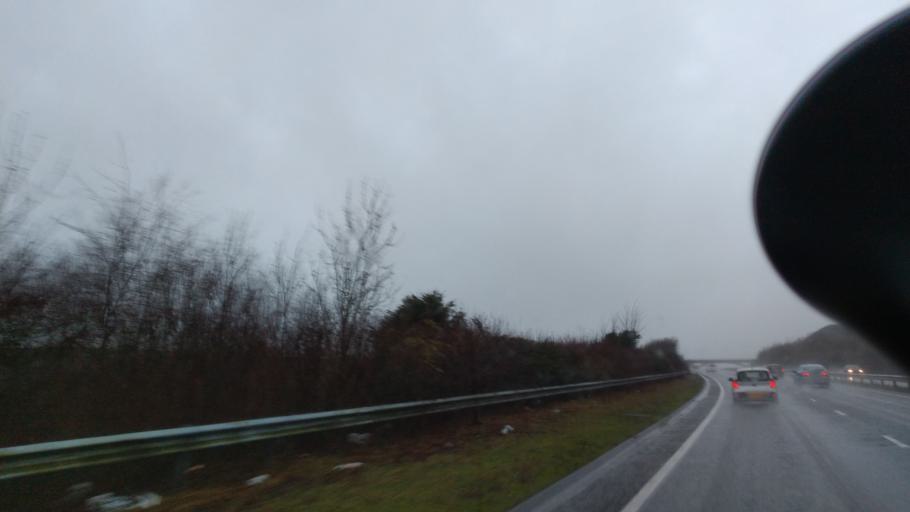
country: GB
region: England
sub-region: Brighton and Hove
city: Brighton
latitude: 50.8675
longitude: -0.1119
